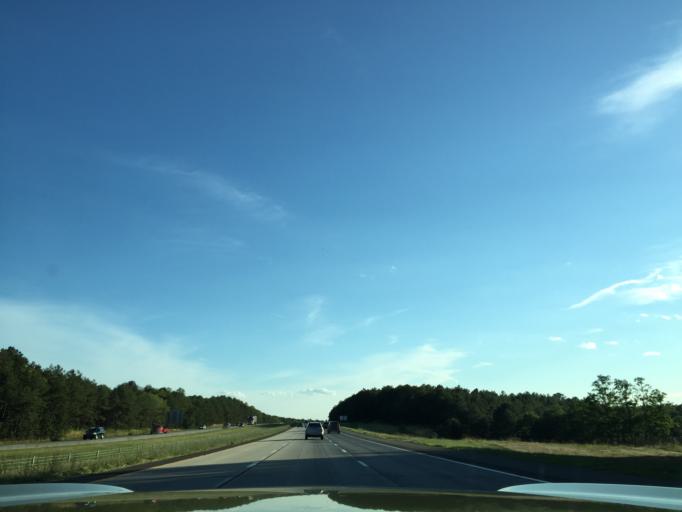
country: US
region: New York
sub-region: Suffolk County
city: Calverton
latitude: 40.8913
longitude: -72.7528
